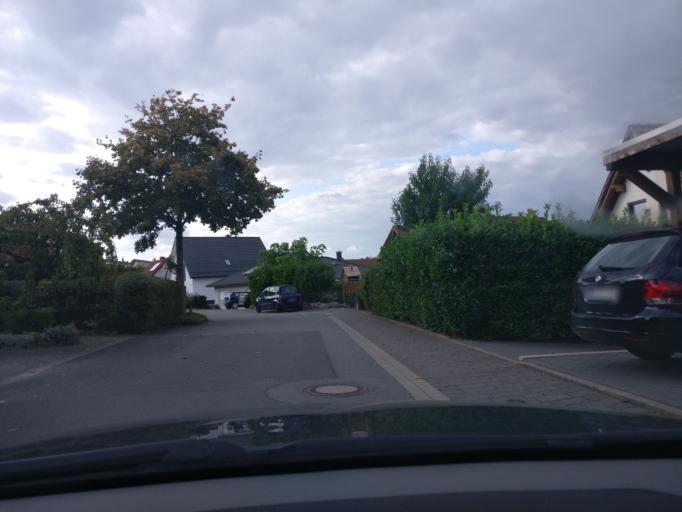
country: DE
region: Lower Saxony
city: Melle
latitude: 52.1910
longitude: 8.3484
